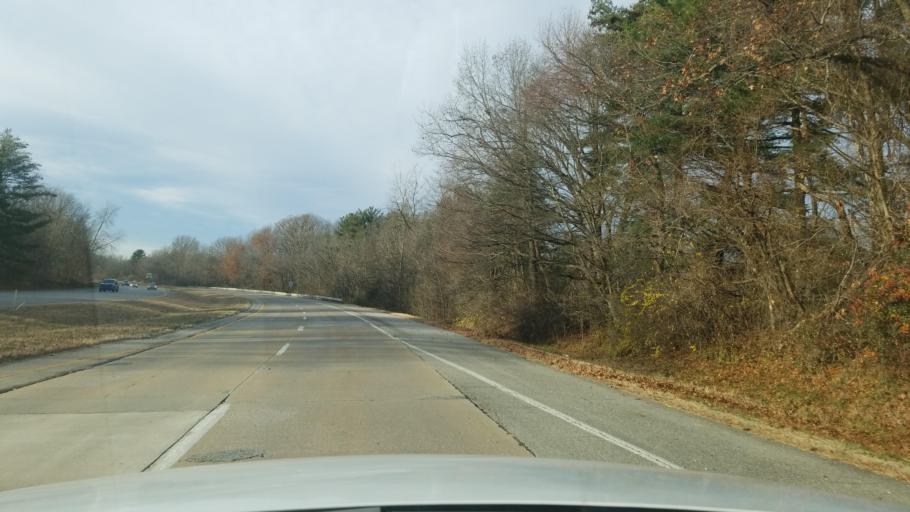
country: US
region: Indiana
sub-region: Vanderburgh County
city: Evansville
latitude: 37.9647
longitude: -87.6874
